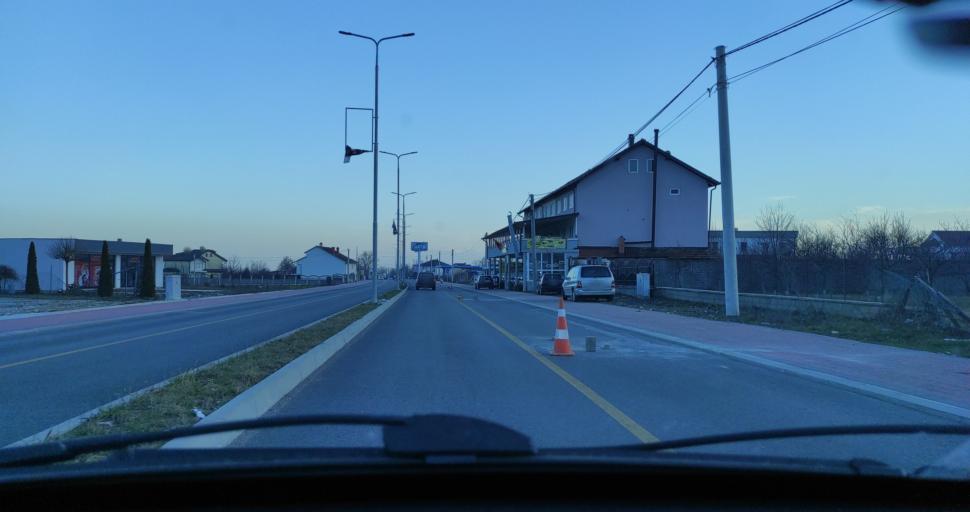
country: XK
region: Gjakova
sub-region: Komuna e Decanit
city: Dranoc
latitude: 42.5246
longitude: 20.3007
